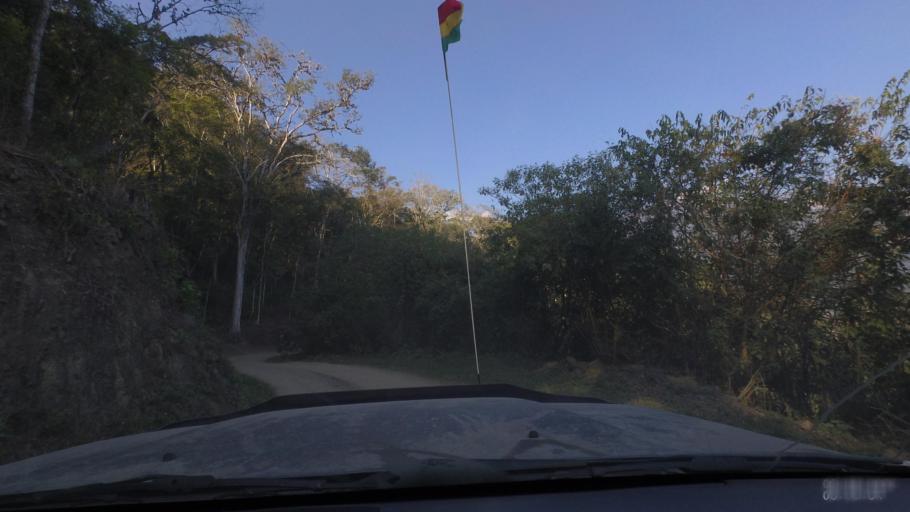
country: BO
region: La Paz
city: Quime
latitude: -16.5086
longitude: -66.7603
